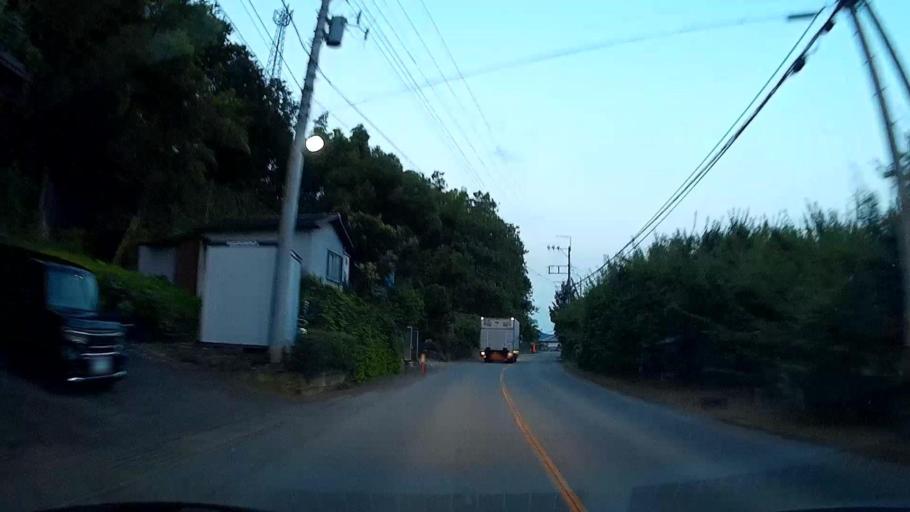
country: JP
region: Gunma
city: Annaka
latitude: 36.3839
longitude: 138.8756
